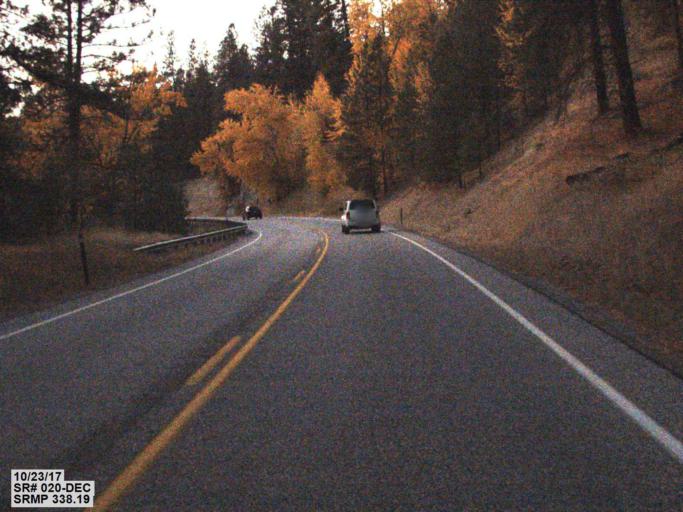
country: US
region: Washington
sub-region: Stevens County
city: Kettle Falls
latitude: 48.5917
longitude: -118.1633
